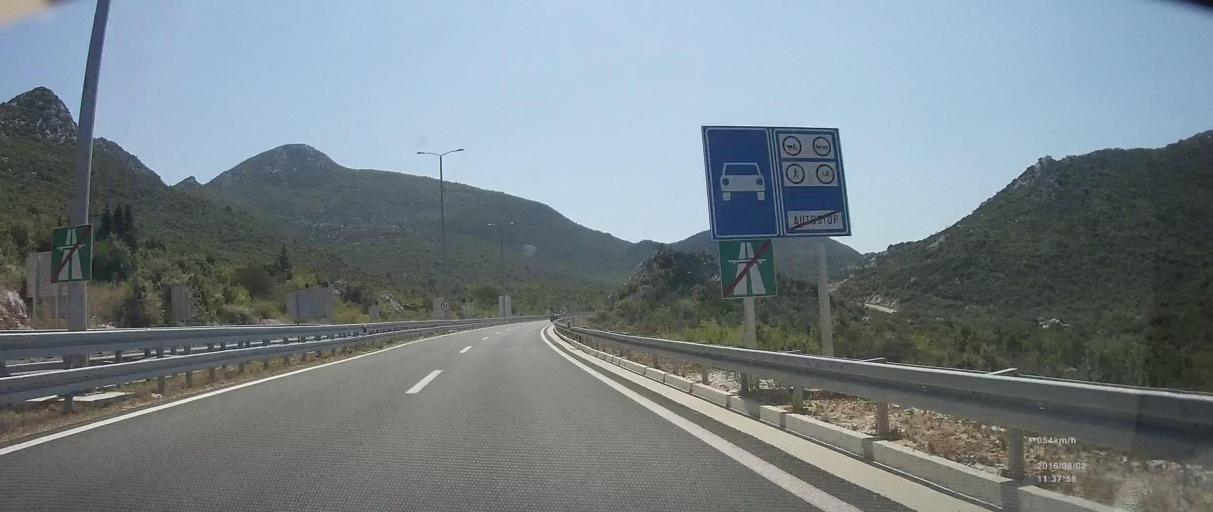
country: HR
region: Dubrovacko-Neretvanska
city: Komin
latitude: 43.1002
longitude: 17.4875
